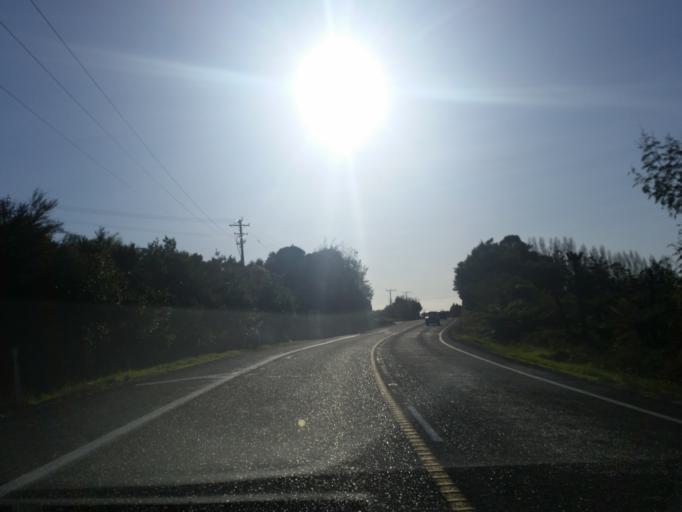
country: NZ
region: Bay of Plenty
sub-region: Western Bay of Plenty District
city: Katikati
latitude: -37.5272
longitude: 175.9147
